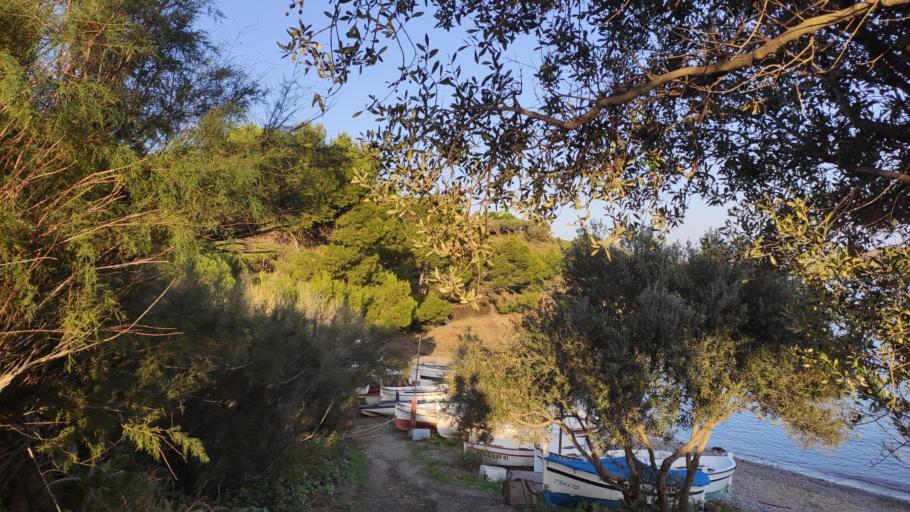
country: ES
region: Catalonia
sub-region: Provincia de Girona
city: Cadaques
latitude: 42.2942
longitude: 3.2890
